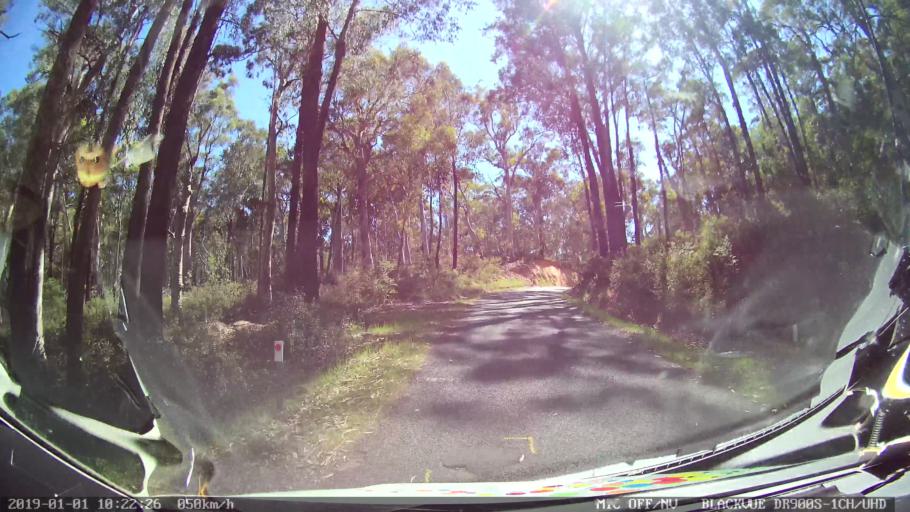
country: AU
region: New South Wales
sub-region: Snowy River
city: Jindabyne
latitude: -36.0779
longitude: 148.2037
